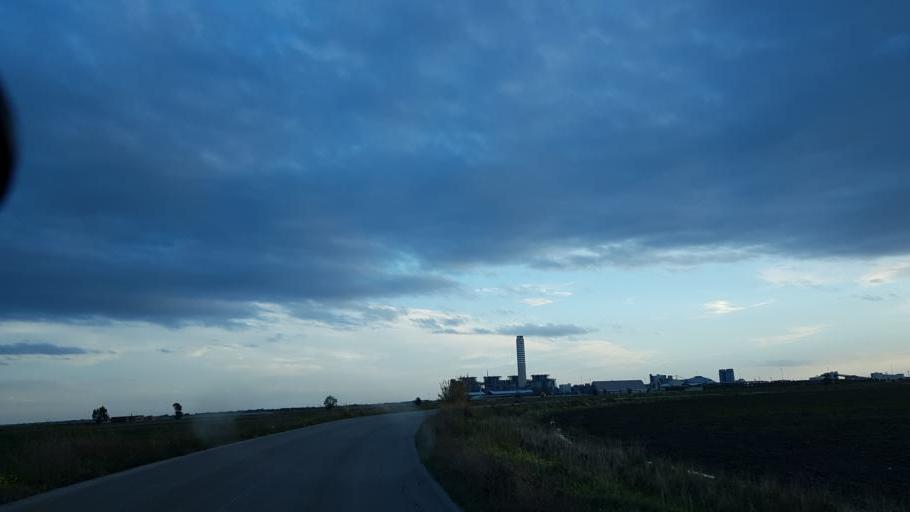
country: IT
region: Apulia
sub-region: Provincia di Brindisi
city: La Rosa
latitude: 40.5836
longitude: 18.0333
